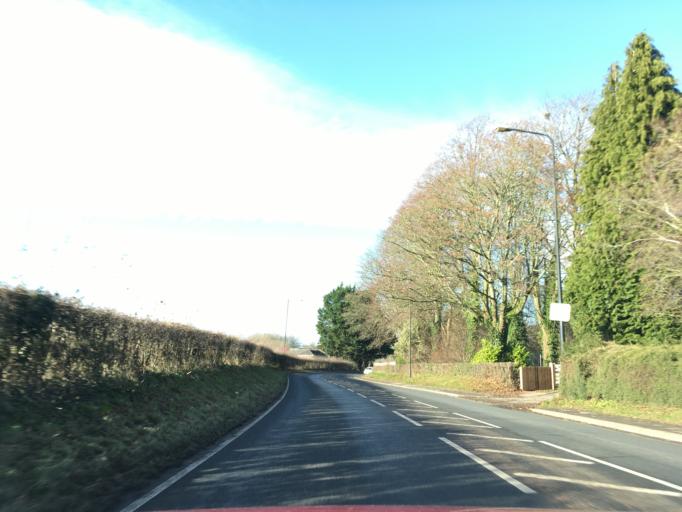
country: GB
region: Wales
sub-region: Monmouthshire
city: Usk
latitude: 51.7108
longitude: -2.9164
